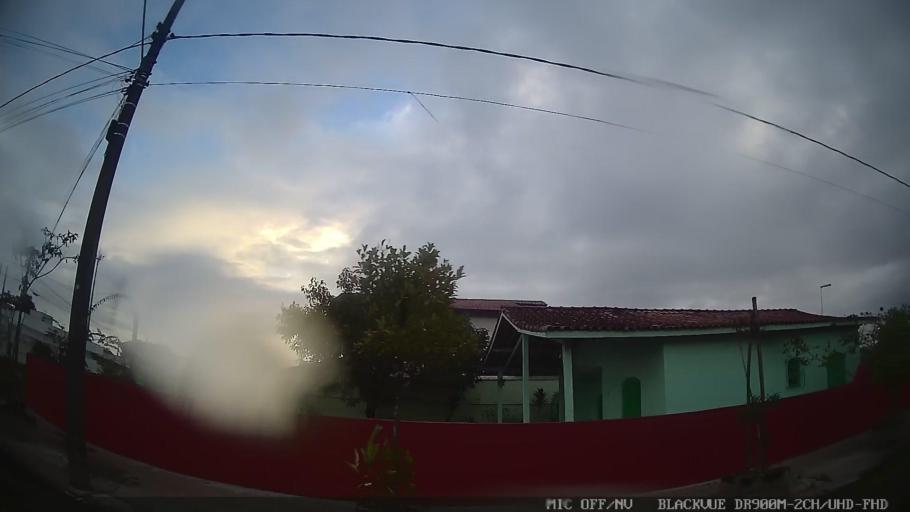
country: BR
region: Sao Paulo
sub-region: Itanhaem
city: Itanhaem
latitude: -24.2017
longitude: -46.8308
